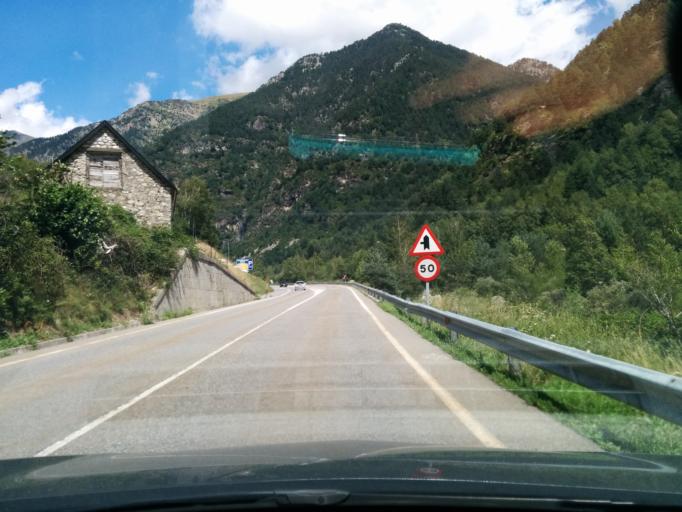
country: ES
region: Aragon
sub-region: Provincia de Huesca
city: Bielsa
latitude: 42.6641
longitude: 0.2108
